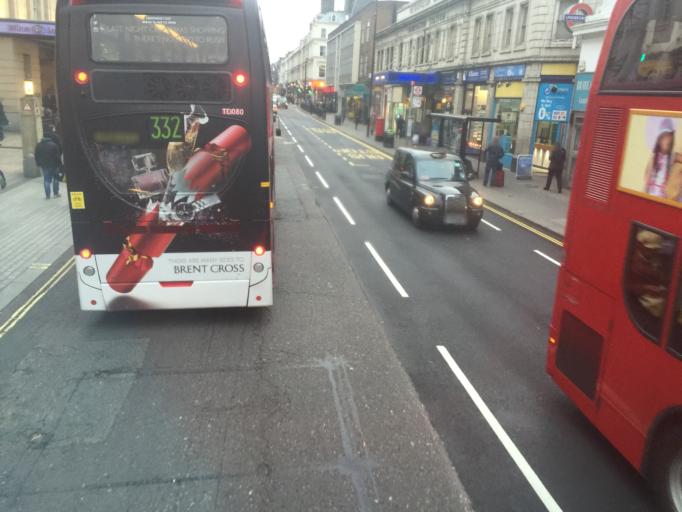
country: GB
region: England
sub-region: Greater London
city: Bayswater
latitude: 51.5154
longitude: -0.1761
